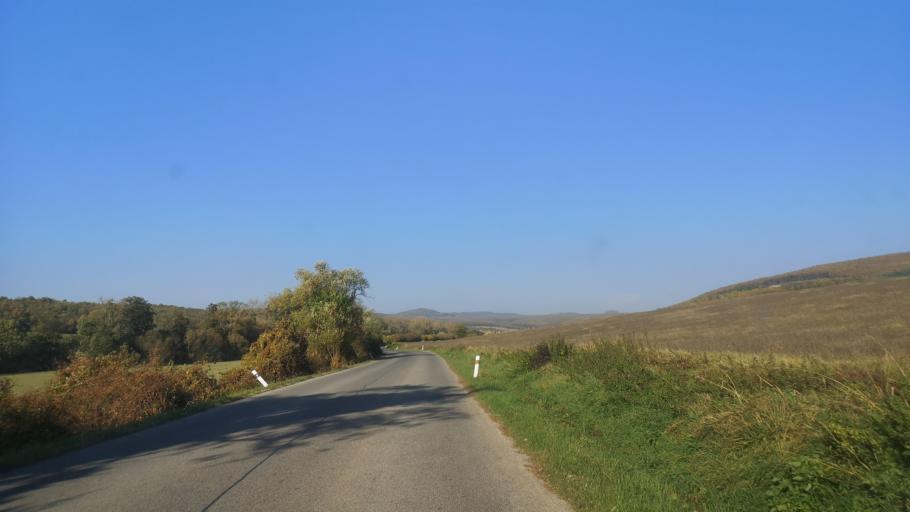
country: SK
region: Nitriansky
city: Zlate Moravce
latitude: 48.4348
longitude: 18.4301
